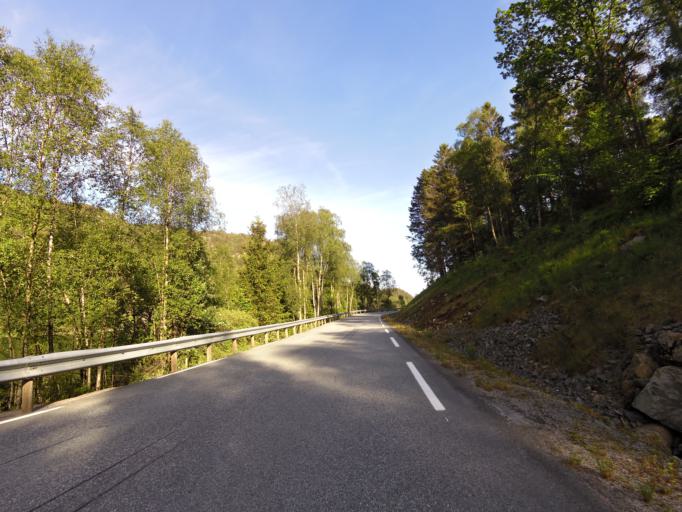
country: NO
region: Vest-Agder
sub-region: Flekkefjord
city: Flekkefjord
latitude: 58.2845
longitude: 6.6170
